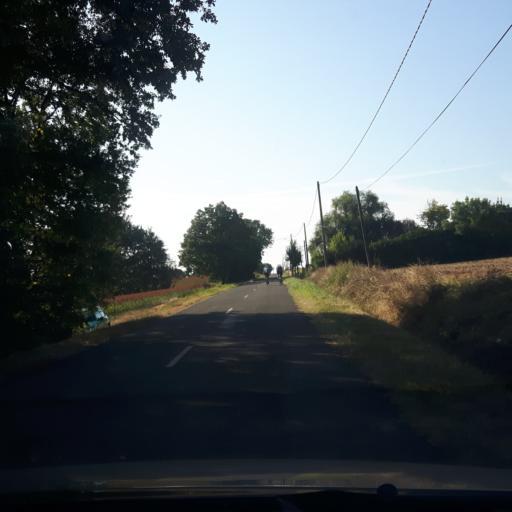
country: FR
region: Midi-Pyrenees
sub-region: Departement de la Haute-Garonne
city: Vacquiers
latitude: 43.7639
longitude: 1.4952
